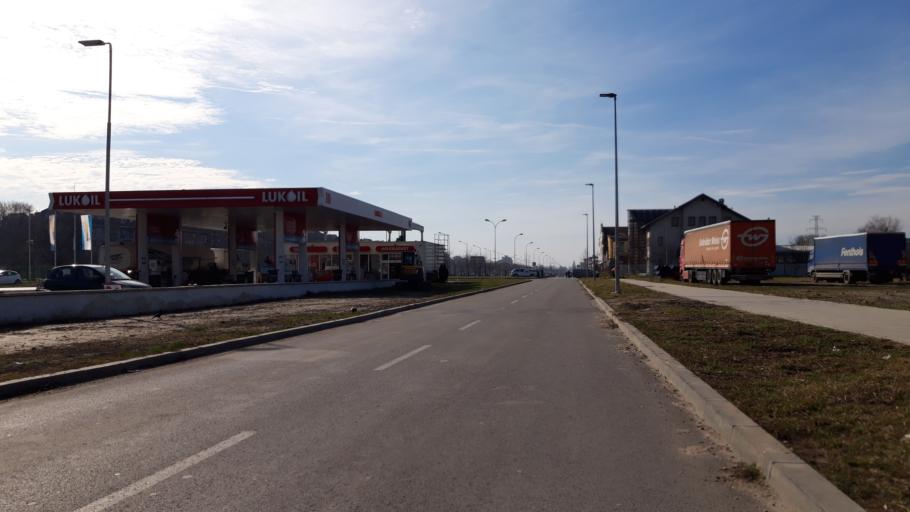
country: RS
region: Autonomna Pokrajina Vojvodina
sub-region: Juznobacki Okrug
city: Novi Sad
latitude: 45.2599
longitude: 19.8062
